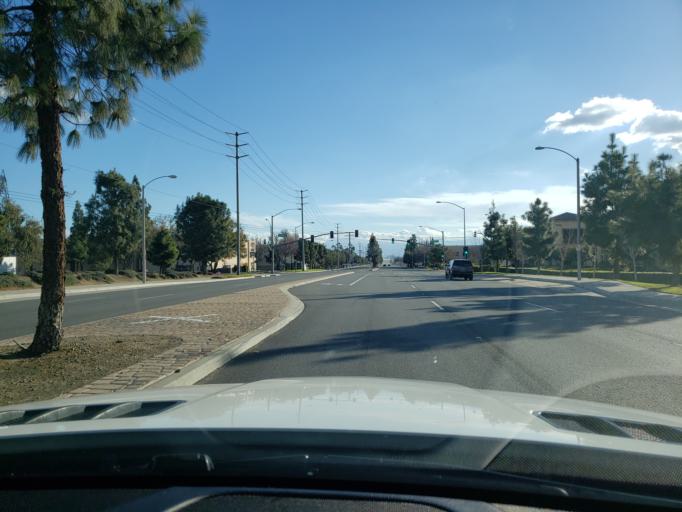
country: US
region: California
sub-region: Riverside County
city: Mira Loma
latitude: 34.0425
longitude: -117.5584
